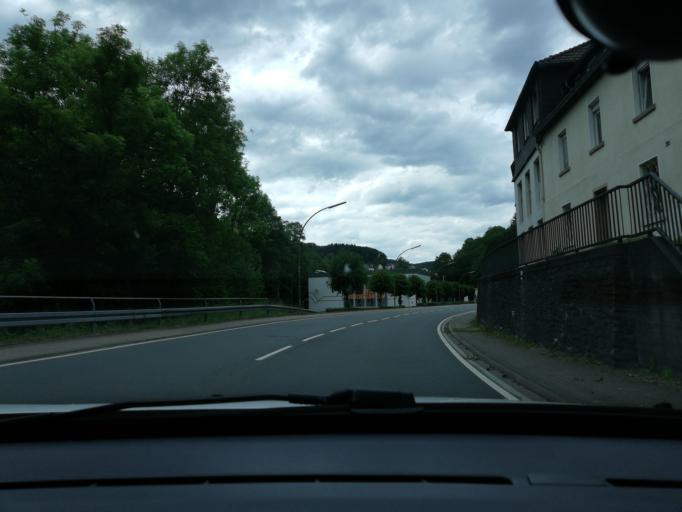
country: DE
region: North Rhine-Westphalia
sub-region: Regierungsbezirk Arnsberg
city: Schalksmuhle
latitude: 51.2467
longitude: 7.5193
